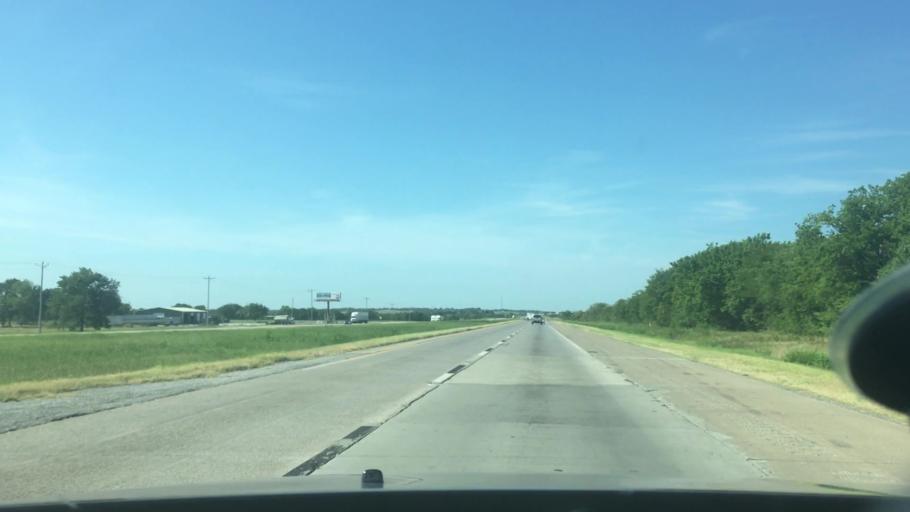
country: US
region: Oklahoma
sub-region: Bryan County
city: Durant
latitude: 34.1757
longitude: -96.2508
